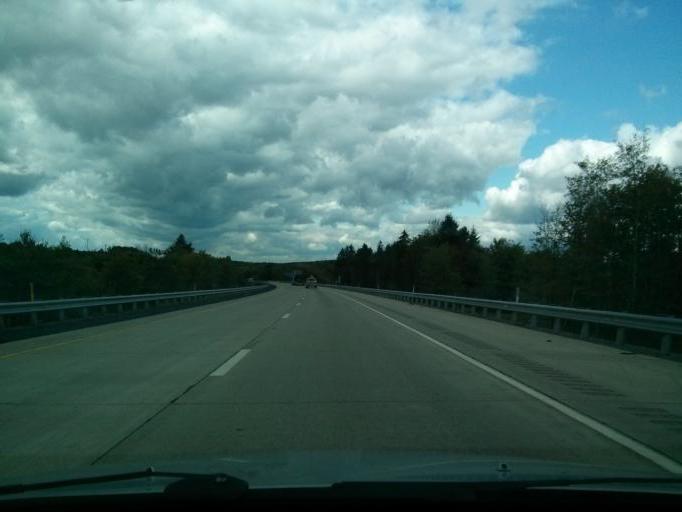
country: US
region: Pennsylvania
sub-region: Jefferson County
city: Reynoldsville
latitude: 41.1526
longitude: -78.9250
